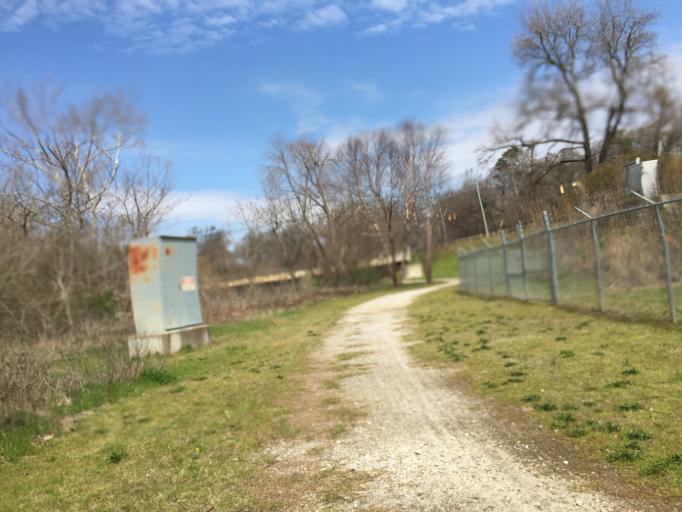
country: US
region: South Carolina
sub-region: Greenville County
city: Mauldin
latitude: 34.7977
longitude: -82.3643
